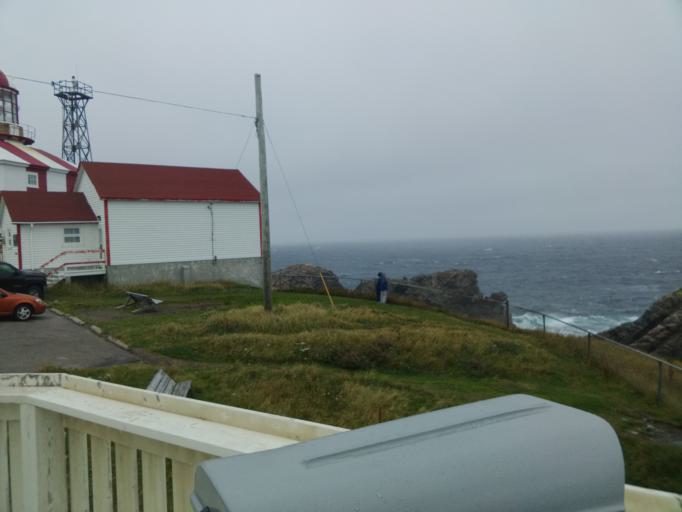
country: CA
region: Newfoundland and Labrador
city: Bonavista
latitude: 48.7011
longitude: -53.0852
